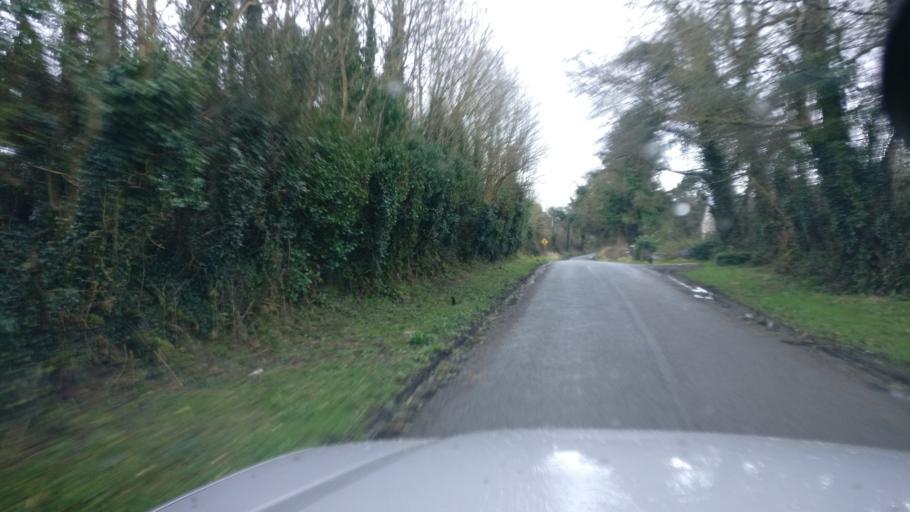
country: IE
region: Connaught
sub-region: County Galway
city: Ballinasloe
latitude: 53.2625
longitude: -8.3564
